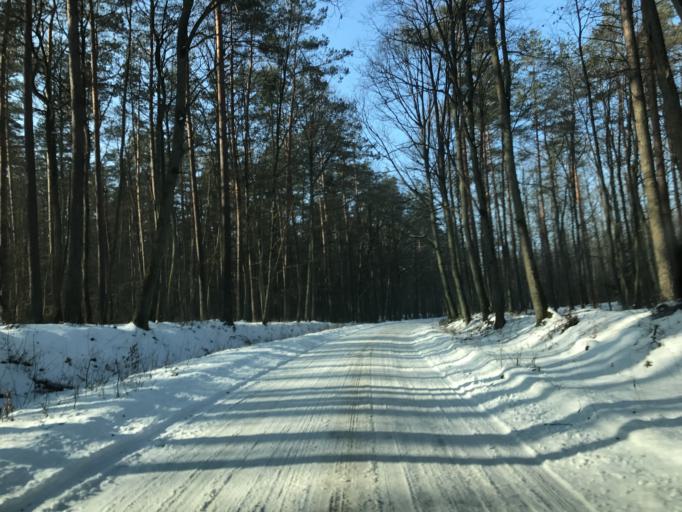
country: PL
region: Kujawsko-Pomorskie
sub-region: Powiat brodnicki
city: Gorzno
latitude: 53.1999
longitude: 19.6969
